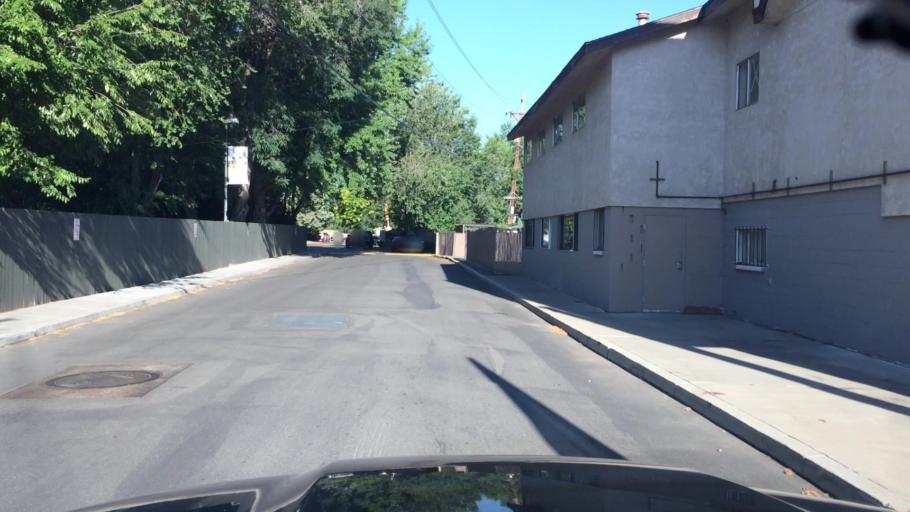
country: US
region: Nevada
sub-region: Washoe County
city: Sparks
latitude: 39.5456
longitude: -119.7528
